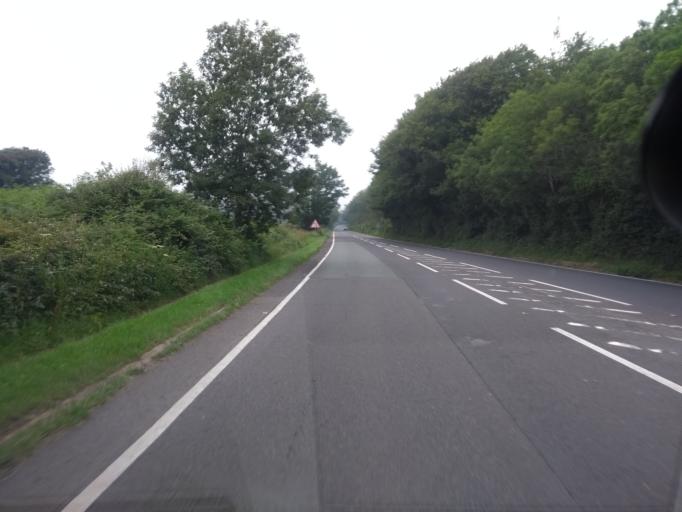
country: GB
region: England
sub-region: Dorset
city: Lyme Regis
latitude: 50.7576
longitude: -2.9408
